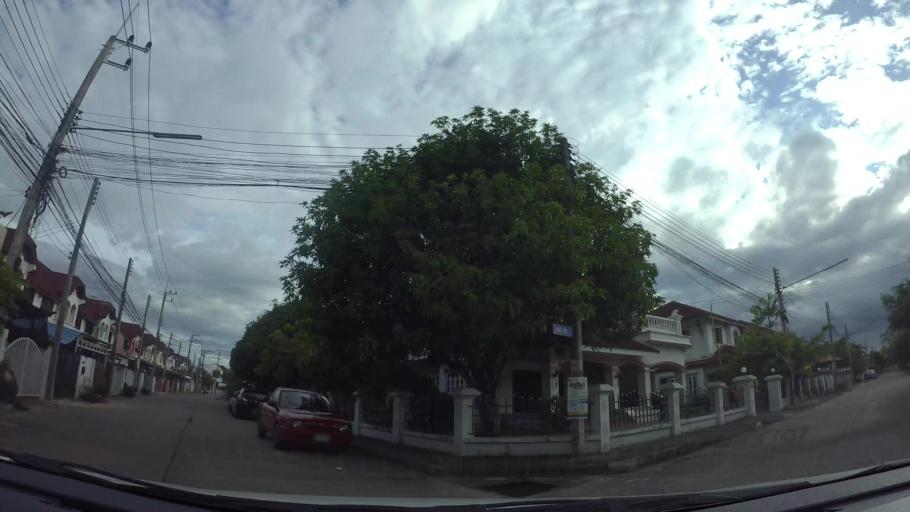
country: TH
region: Chiang Mai
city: Saraphi
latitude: 18.7397
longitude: 99.0313
